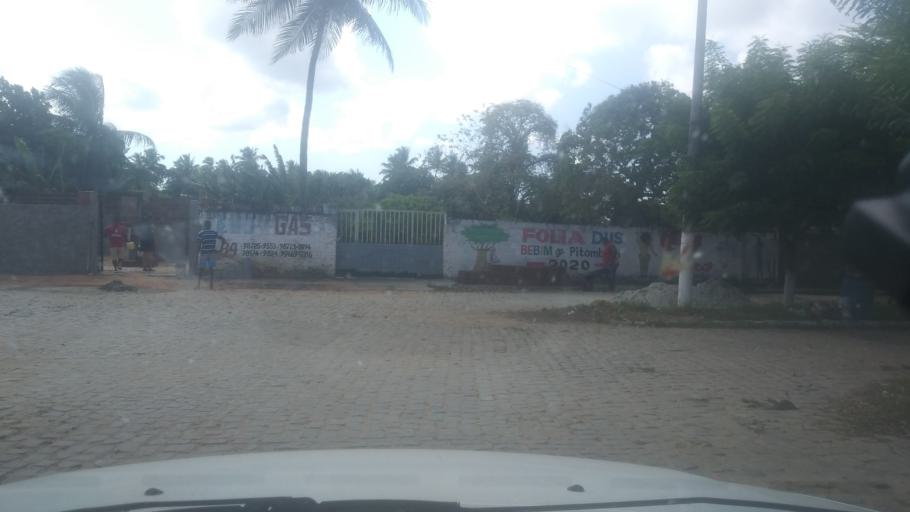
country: BR
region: Rio Grande do Norte
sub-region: Extremoz
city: Extremoz
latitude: -5.7073
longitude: -35.3060
